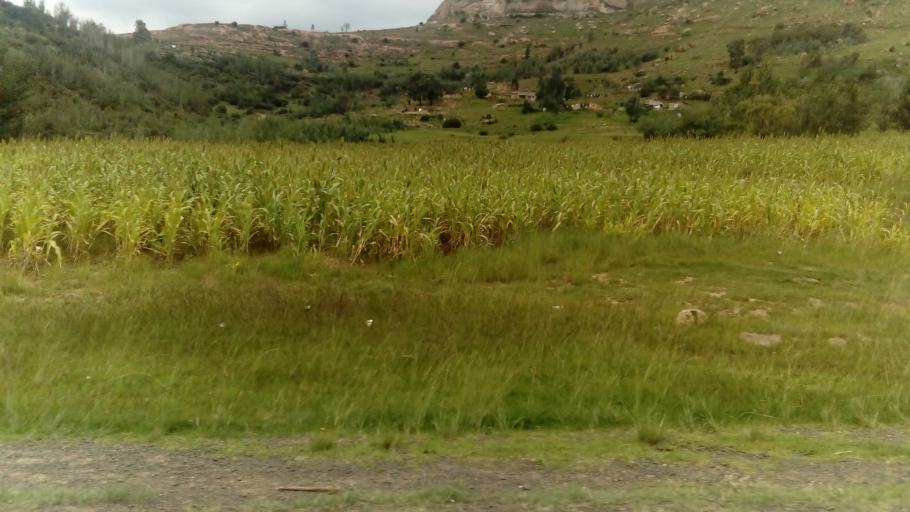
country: LS
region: Leribe
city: Leribe
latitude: -28.9574
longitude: 28.1729
